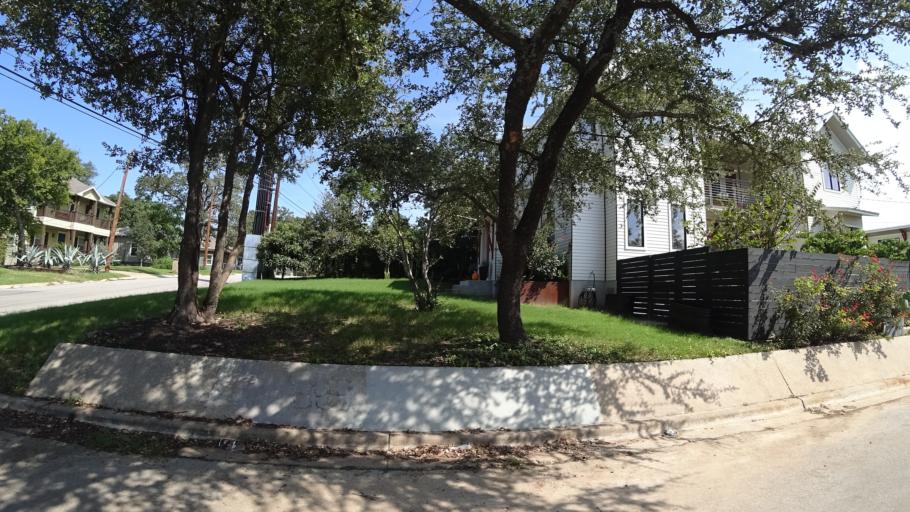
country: US
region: Texas
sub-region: Travis County
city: Austin
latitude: 30.2710
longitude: -97.7173
